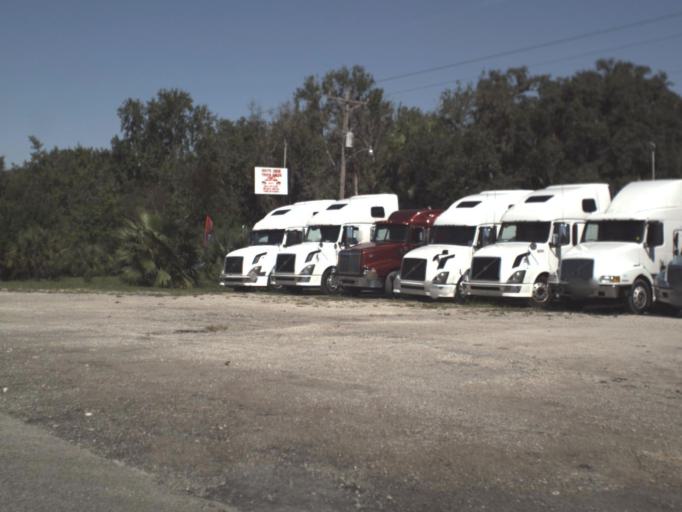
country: US
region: Florida
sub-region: Hendry County
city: Port LaBelle
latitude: 26.9530
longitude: -81.3164
